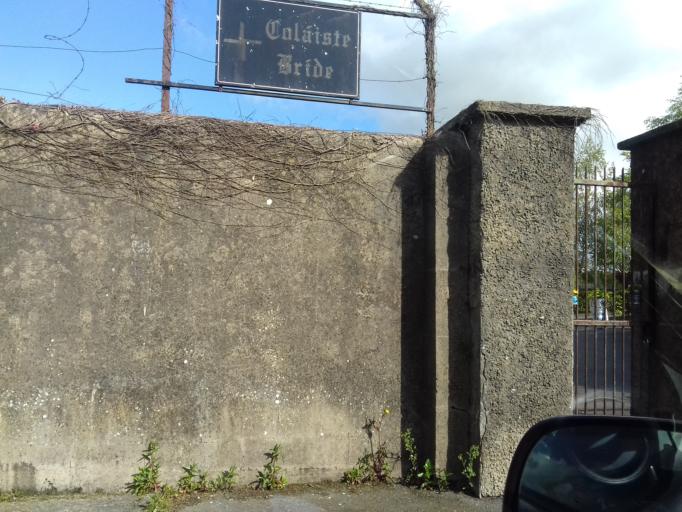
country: IE
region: Leinster
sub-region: Loch Garman
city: Enniscorthy
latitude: 52.5020
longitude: -6.5595
